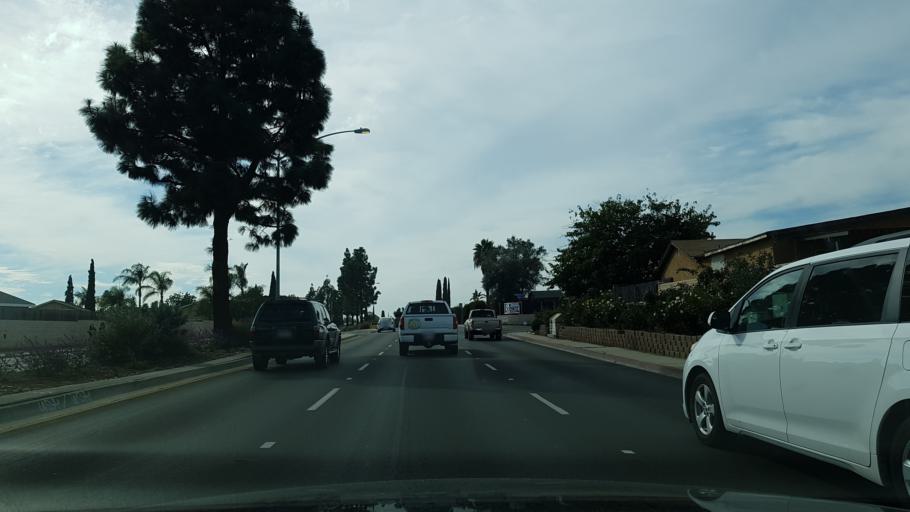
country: US
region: California
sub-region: San Diego County
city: Fairbanks Ranch
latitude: 32.9121
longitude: -117.1514
